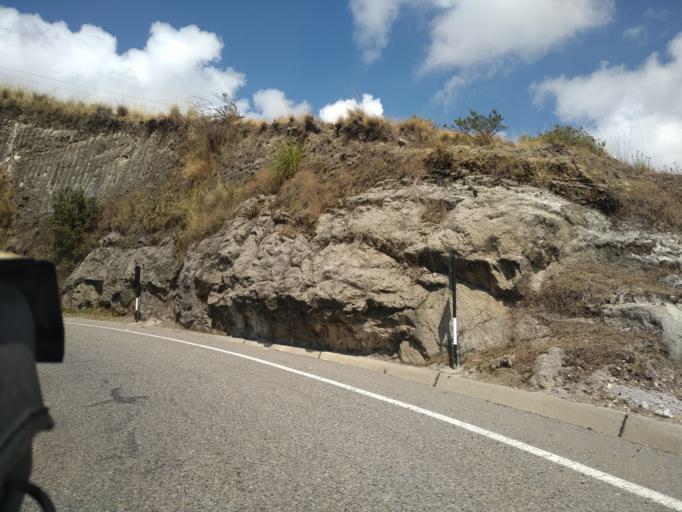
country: PE
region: La Libertad
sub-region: Provincia de Santiago de Chuco
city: Quiruvilca
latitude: -7.9181
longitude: -78.1531
